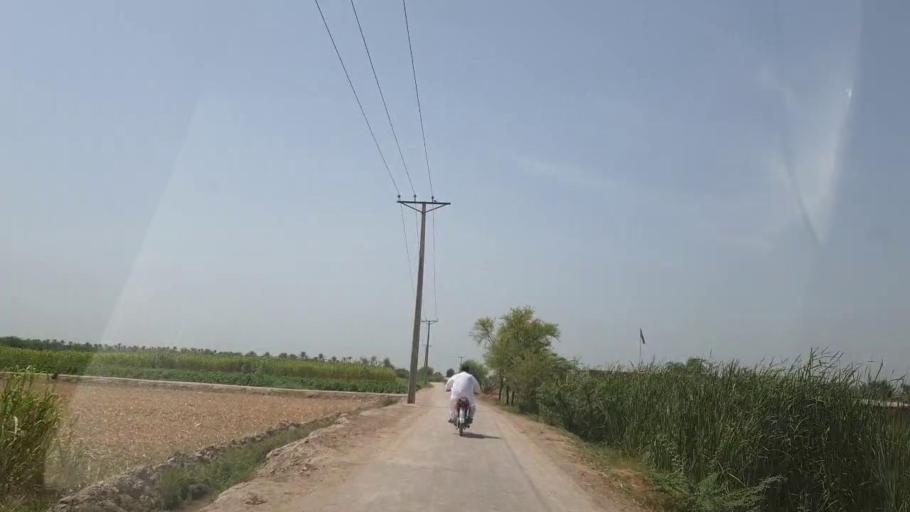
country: PK
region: Sindh
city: Gambat
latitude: 27.3114
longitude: 68.5480
